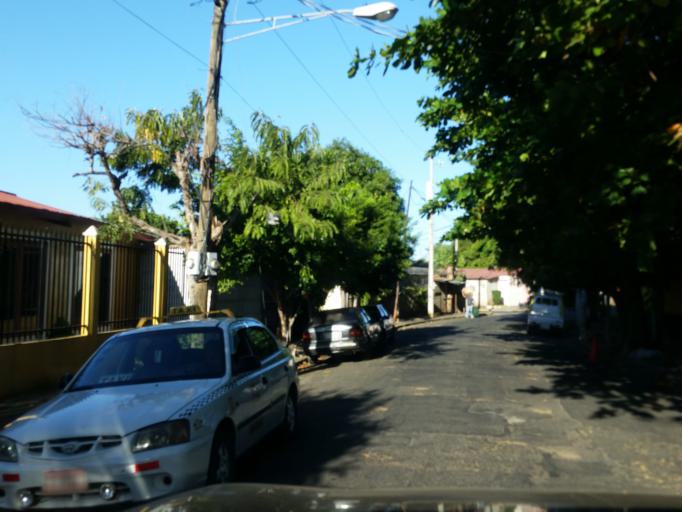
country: NI
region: Managua
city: Managua
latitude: 12.1406
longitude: -86.2791
